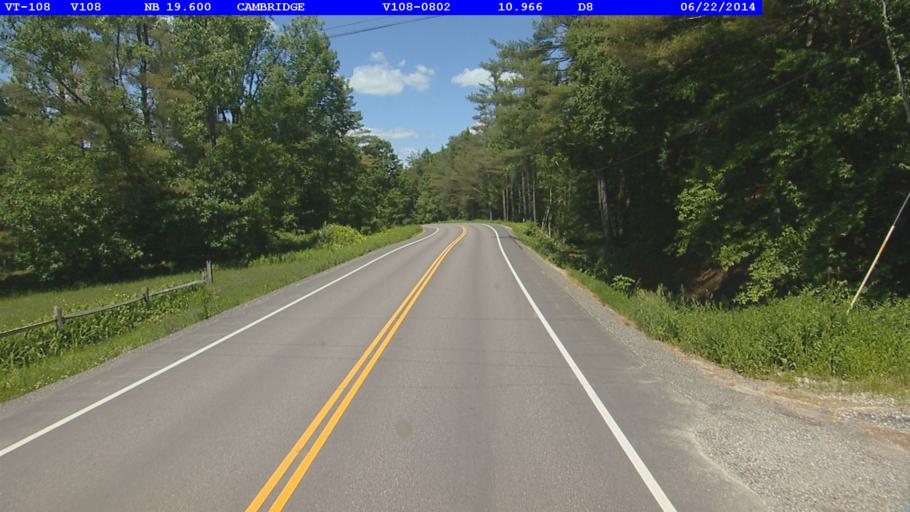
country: US
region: Vermont
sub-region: Lamoille County
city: Johnson
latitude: 44.6735
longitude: -72.8257
